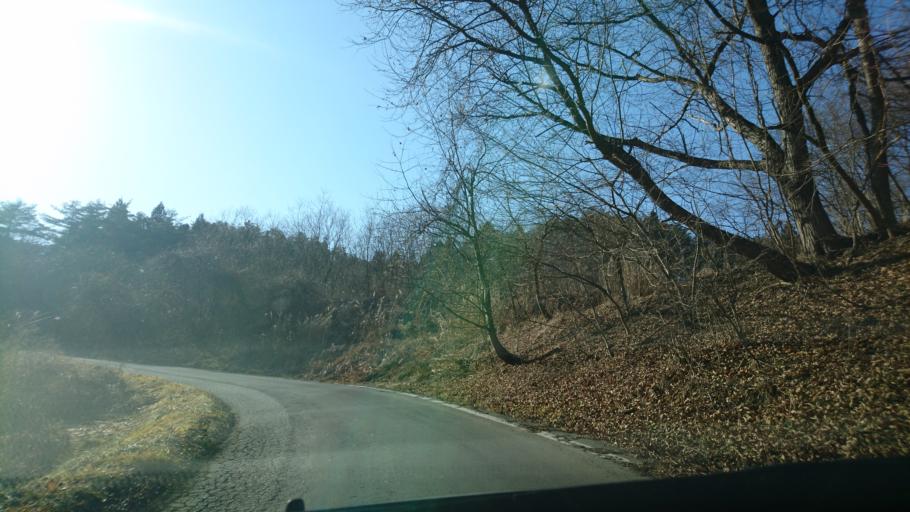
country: JP
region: Iwate
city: Ichinoseki
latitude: 38.8133
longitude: 141.2770
